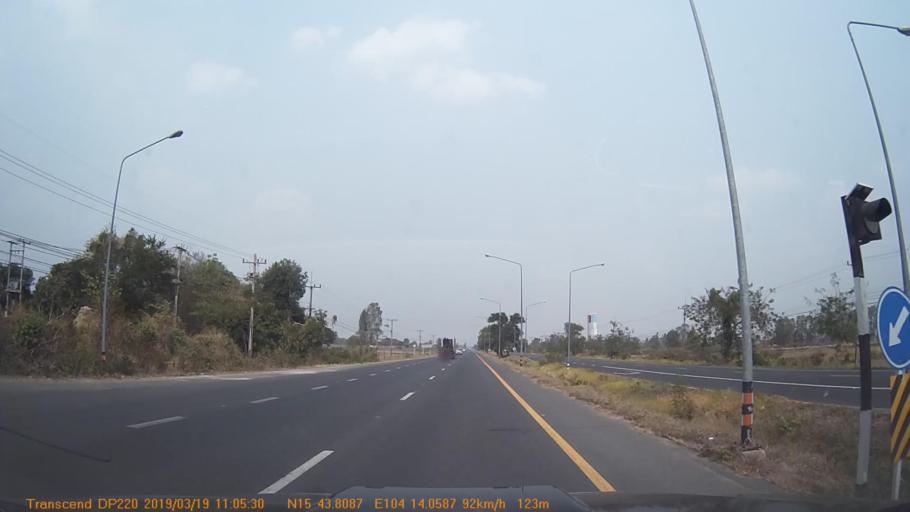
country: TH
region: Yasothon
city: Kham Khuean Kaeo
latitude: 15.7303
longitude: 104.2342
